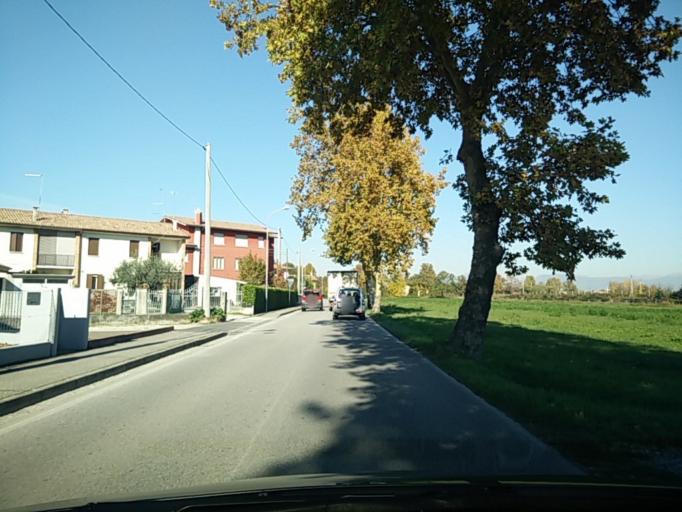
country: IT
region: Veneto
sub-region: Provincia di Treviso
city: Varago
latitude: 45.7216
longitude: 12.2936
